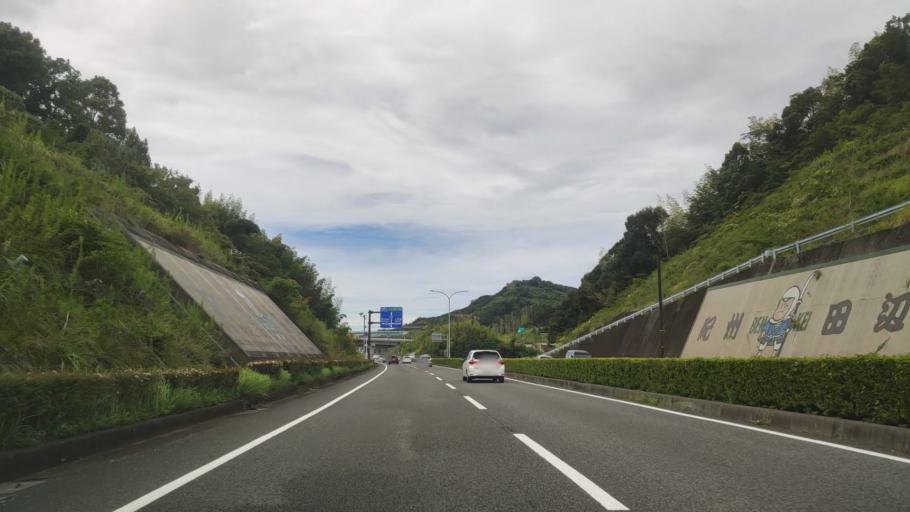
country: JP
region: Wakayama
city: Tanabe
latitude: 33.7449
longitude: 135.3810
